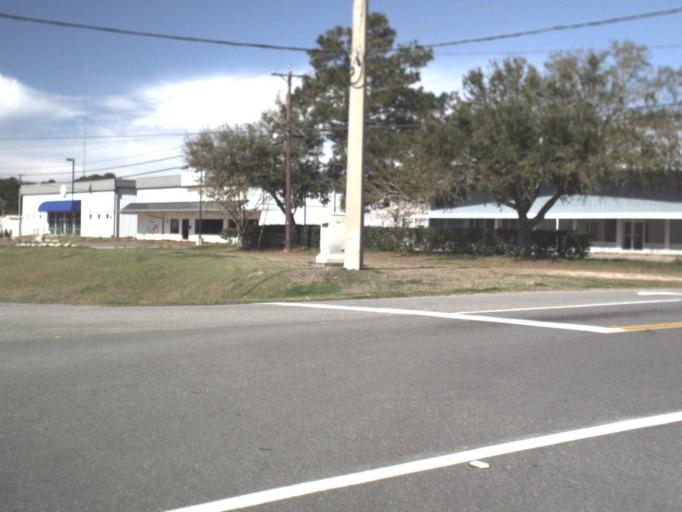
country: US
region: Florida
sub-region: Leon County
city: Tallahassee
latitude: 30.4400
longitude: -84.3418
